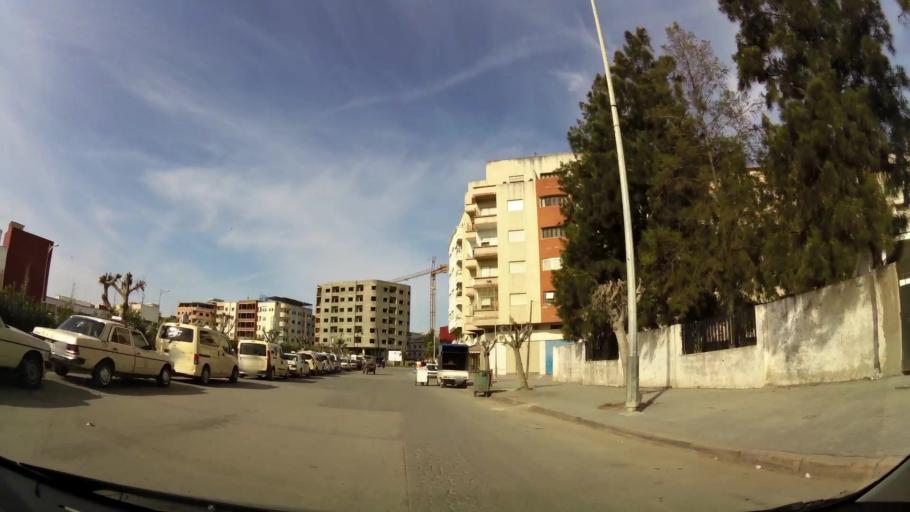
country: MA
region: Tanger-Tetouan
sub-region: Tanger-Assilah
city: Tangier
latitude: 35.7365
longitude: -5.8005
